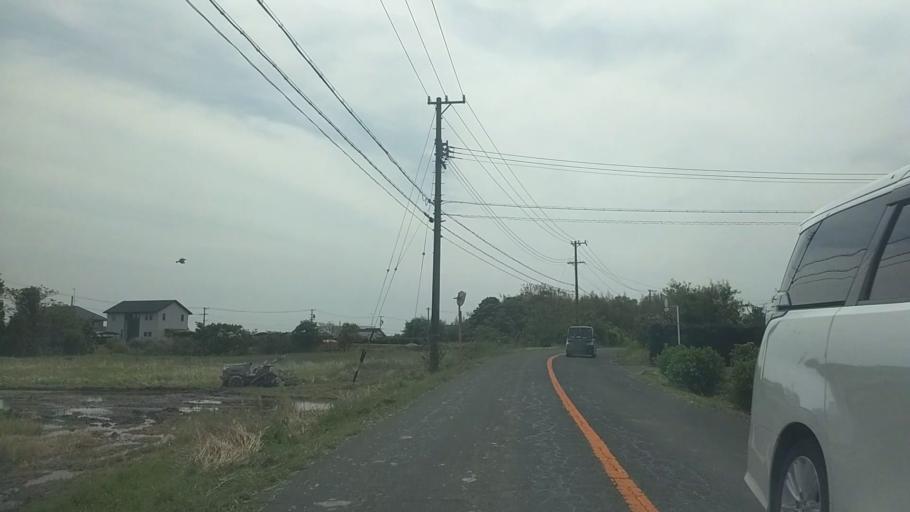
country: JP
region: Shizuoka
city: Kosai-shi
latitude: 34.7381
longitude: 137.5391
